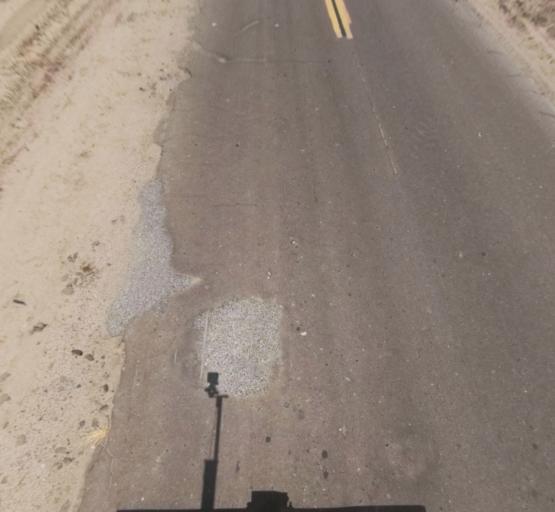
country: US
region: California
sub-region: Fresno County
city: Biola
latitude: 36.8296
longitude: -120.0979
